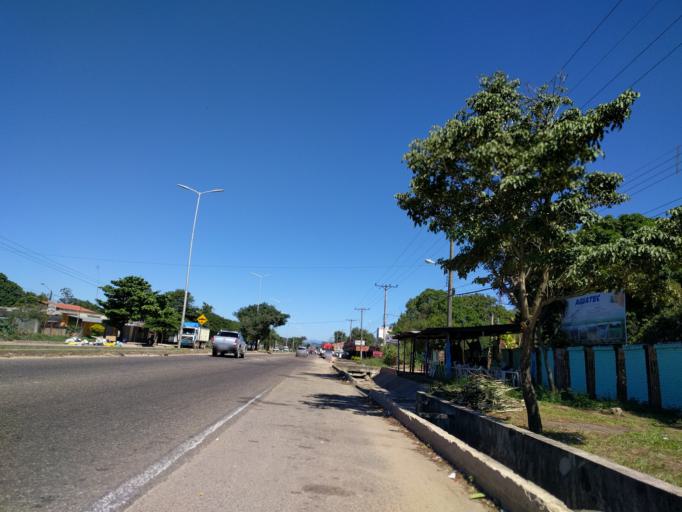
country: BO
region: Santa Cruz
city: Santa Cruz de la Sierra
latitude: -17.8613
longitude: -63.2643
